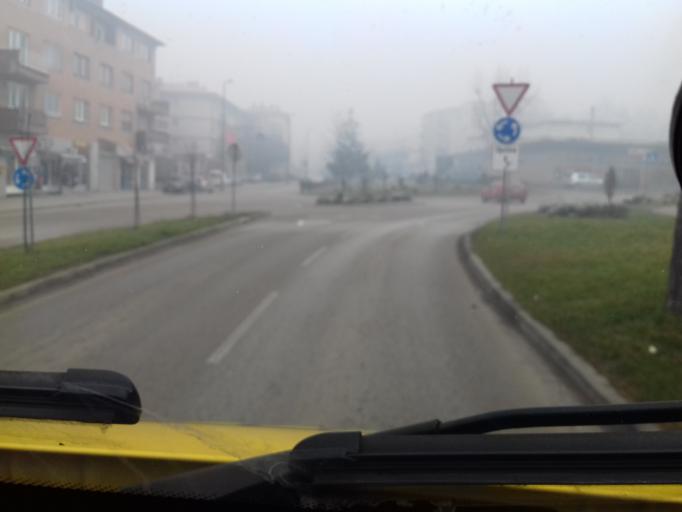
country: BA
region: Federation of Bosnia and Herzegovina
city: Kakanj
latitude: 44.1243
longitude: 18.1150
